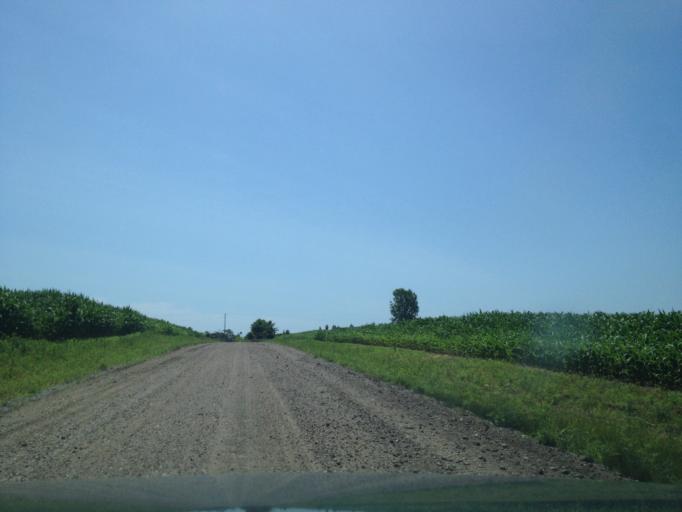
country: CA
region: Ontario
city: Aylmer
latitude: 42.6422
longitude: -80.7706
